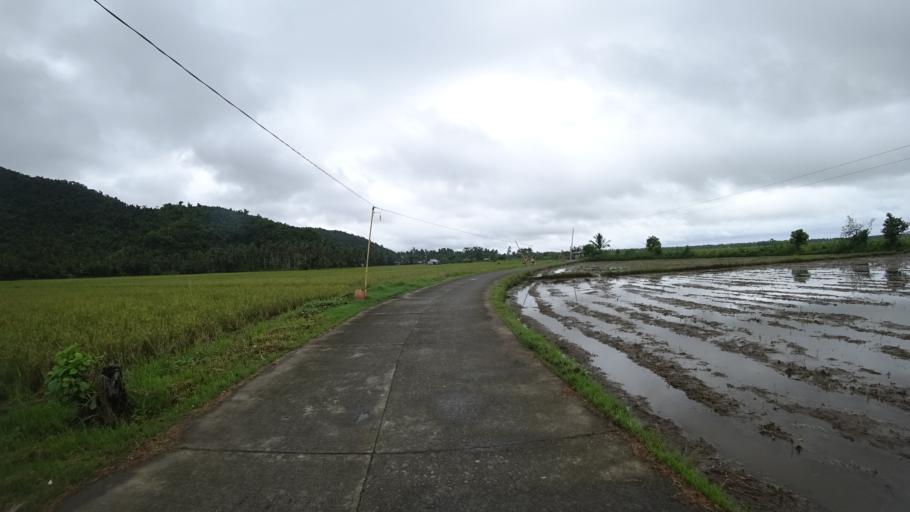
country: PH
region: Eastern Visayas
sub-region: Province of Leyte
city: Bugho
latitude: 10.7928
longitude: 124.9736
